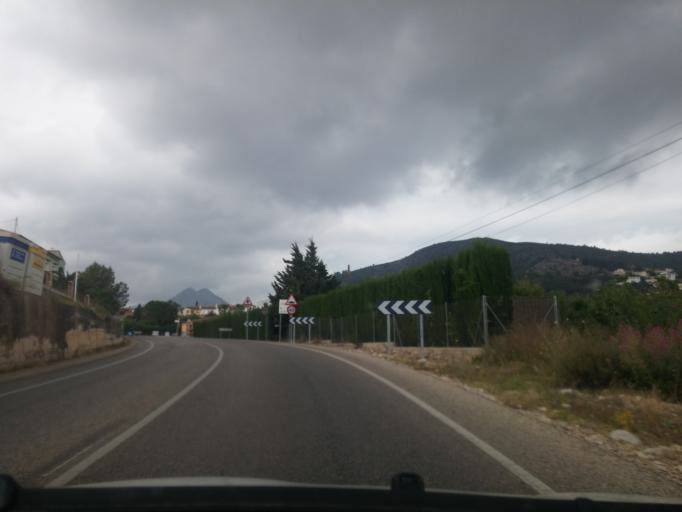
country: ES
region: Valencia
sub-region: Provincia de Alicante
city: Alcalali
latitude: 38.7495
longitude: -0.0364
